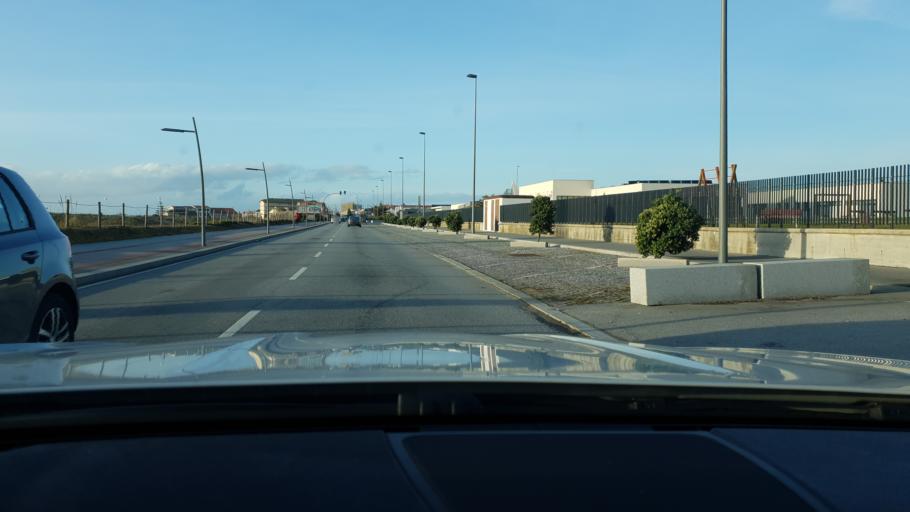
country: PT
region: Porto
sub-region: Matosinhos
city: Lavra
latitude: 41.2323
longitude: -8.7199
